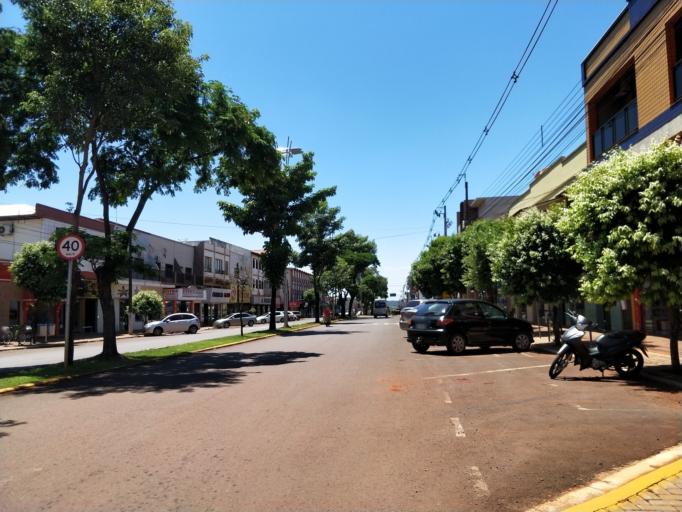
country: BR
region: Parana
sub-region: Marechal Candido Rondon
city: Marechal Candido Rondon
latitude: -24.5636
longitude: -54.0615
